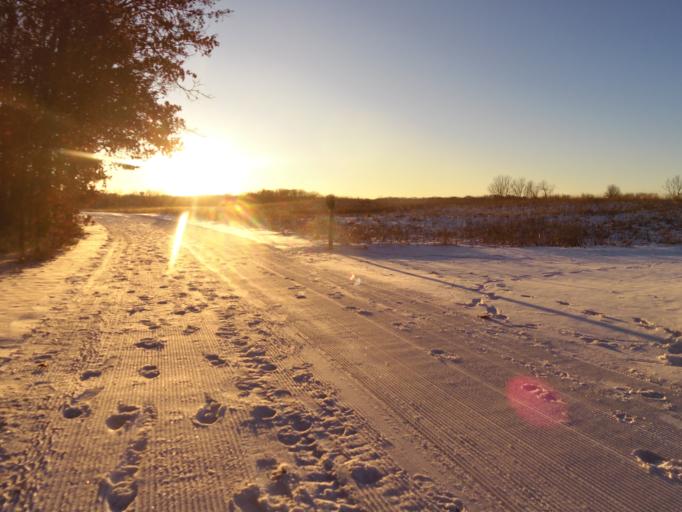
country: US
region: Minnesota
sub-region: Washington County
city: Lake Elmo
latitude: 44.9834
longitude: -92.9084
